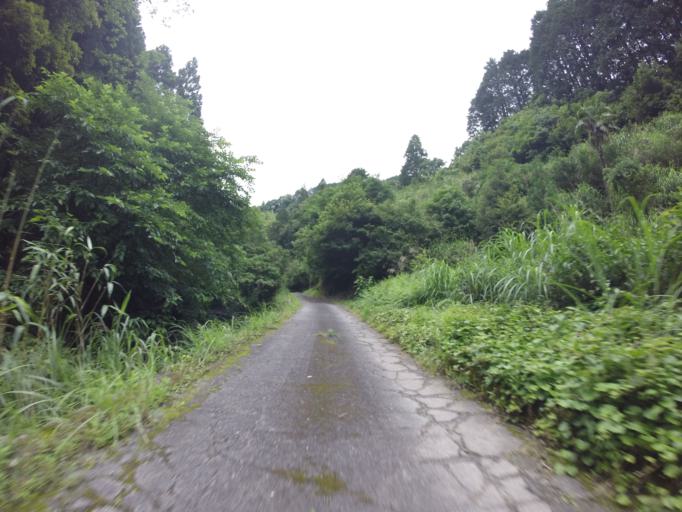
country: JP
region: Shizuoka
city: Shizuoka-shi
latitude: 35.0260
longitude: 138.3056
